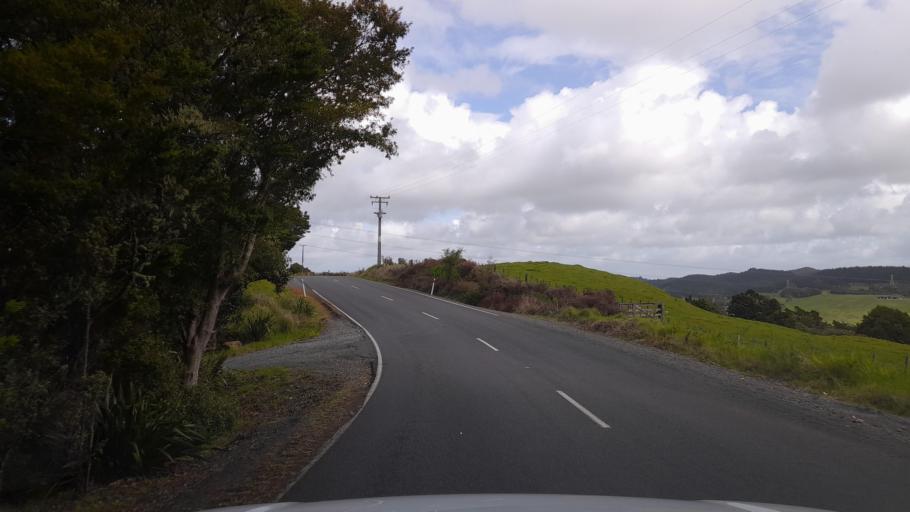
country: NZ
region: Northland
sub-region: Whangarei
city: Maungatapere
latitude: -35.7599
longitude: 174.2373
